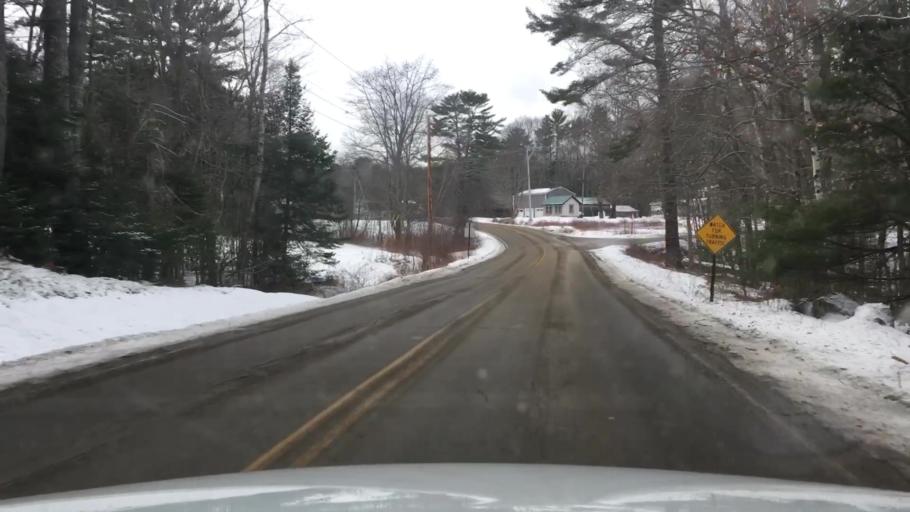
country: US
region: Maine
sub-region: Waldo County
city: Lincolnville
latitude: 44.2883
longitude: -69.0286
